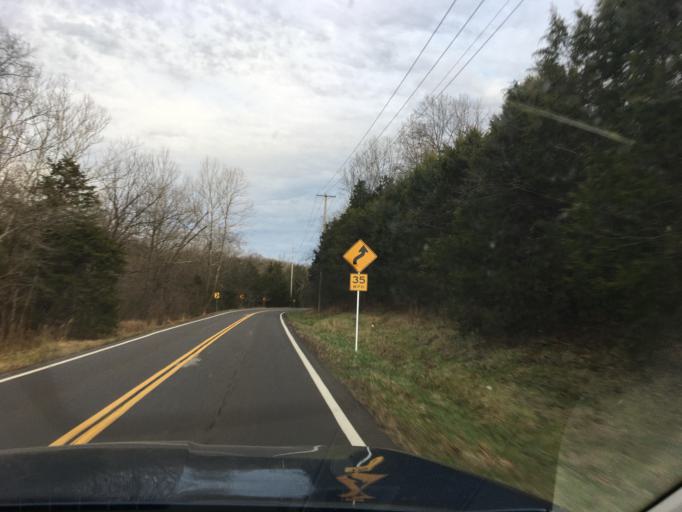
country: US
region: Missouri
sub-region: Jefferson County
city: De Soto
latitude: 38.1075
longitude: -90.5621
